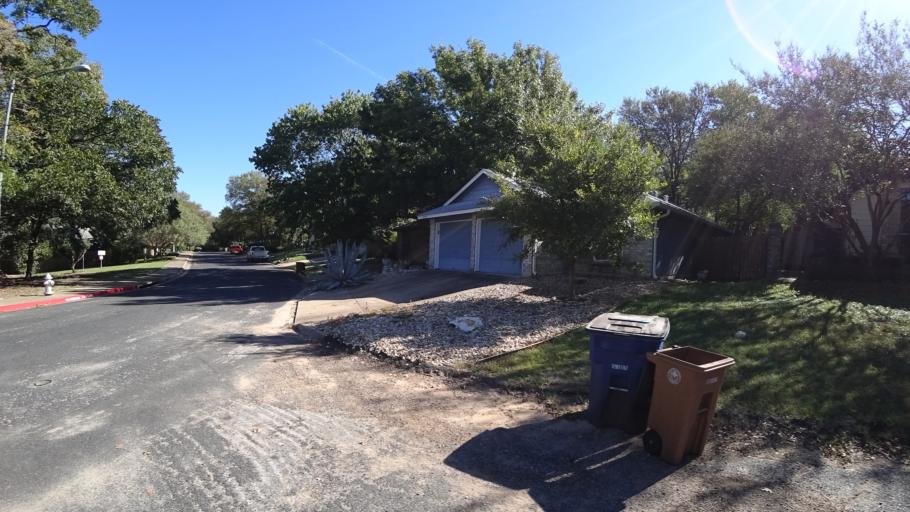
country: US
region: Texas
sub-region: Travis County
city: Austin
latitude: 30.2304
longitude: -97.7108
